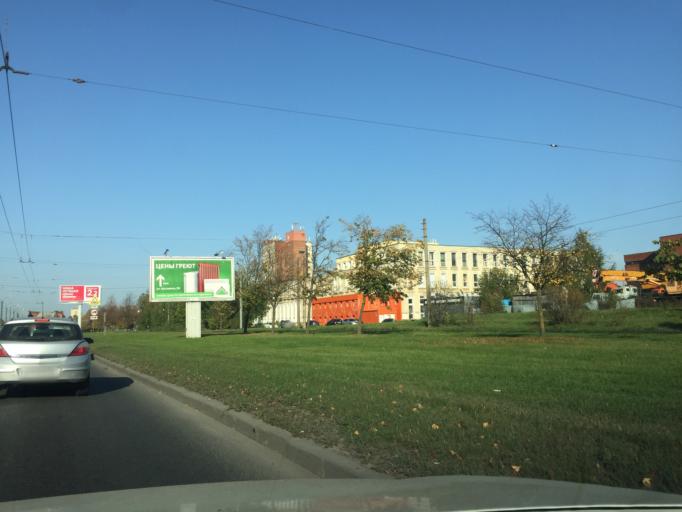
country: RU
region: Leningrad
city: Akademicheskoe
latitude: 60.0004
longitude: 30.4372
